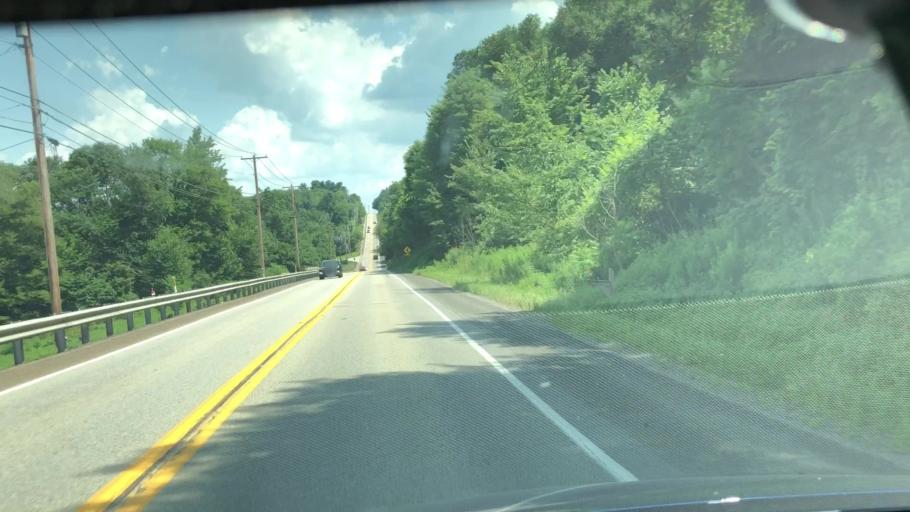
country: US
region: Pennsylvania
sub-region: Armstrong County
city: Freeport
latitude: 40.7107
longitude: -79.7384
